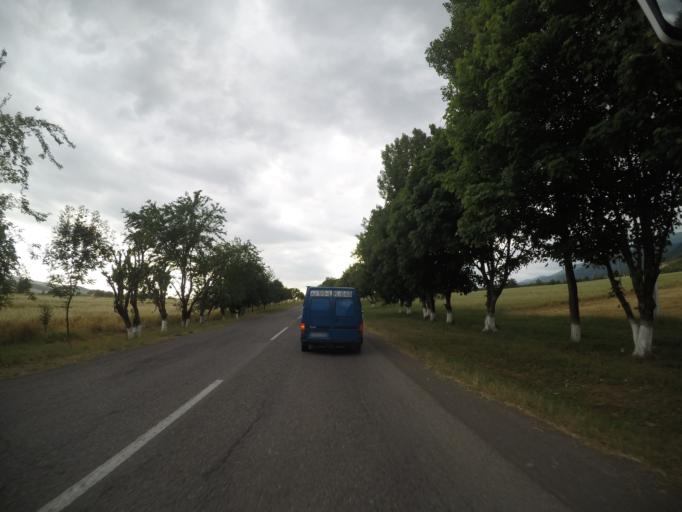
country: AZ
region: Ismayilli
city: Ismayilli
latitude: 40.7730
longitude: 48.2024
